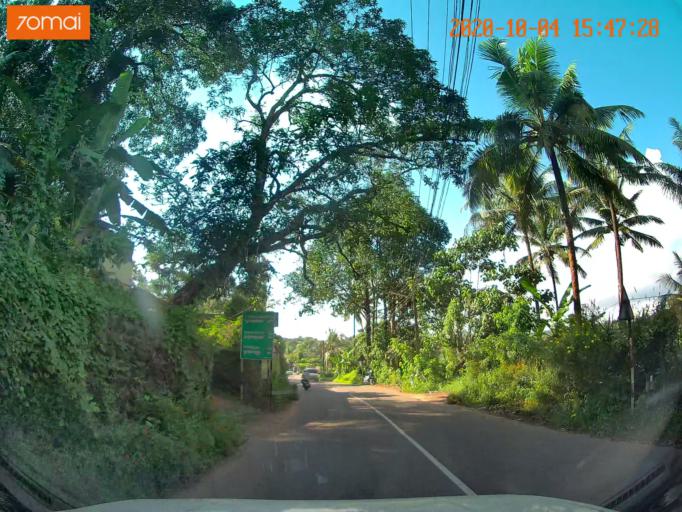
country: IN
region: Kerala
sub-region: Kottayam
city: Palackattumala
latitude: 9.7623
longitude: 76.5676
